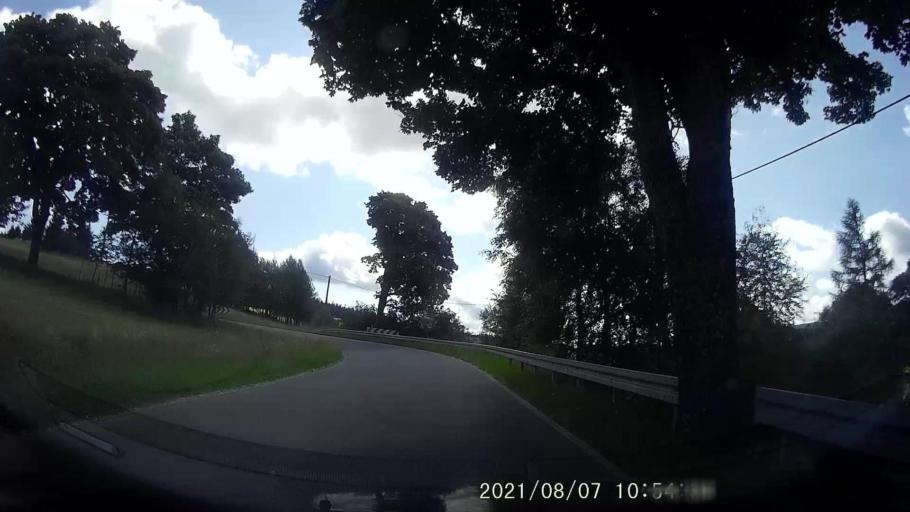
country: CZ
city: Rokytnice v Orlickych Horach
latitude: 50.2722
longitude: 16.4859
